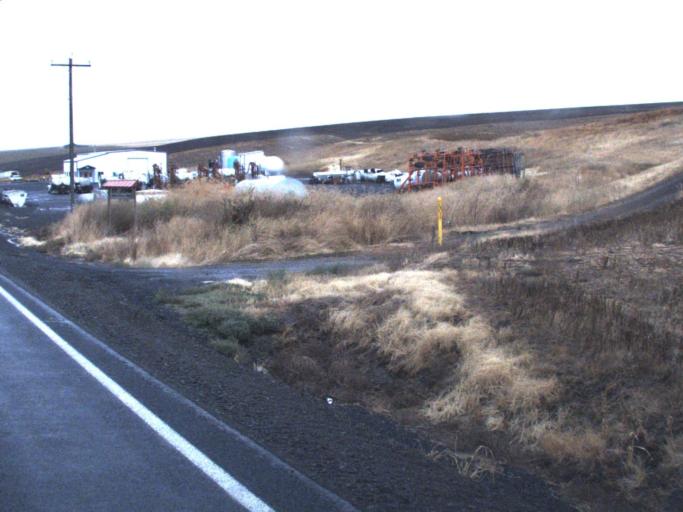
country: US
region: Washington
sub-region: Whitman County
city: Colfax
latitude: 47.0900
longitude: -117.5681
